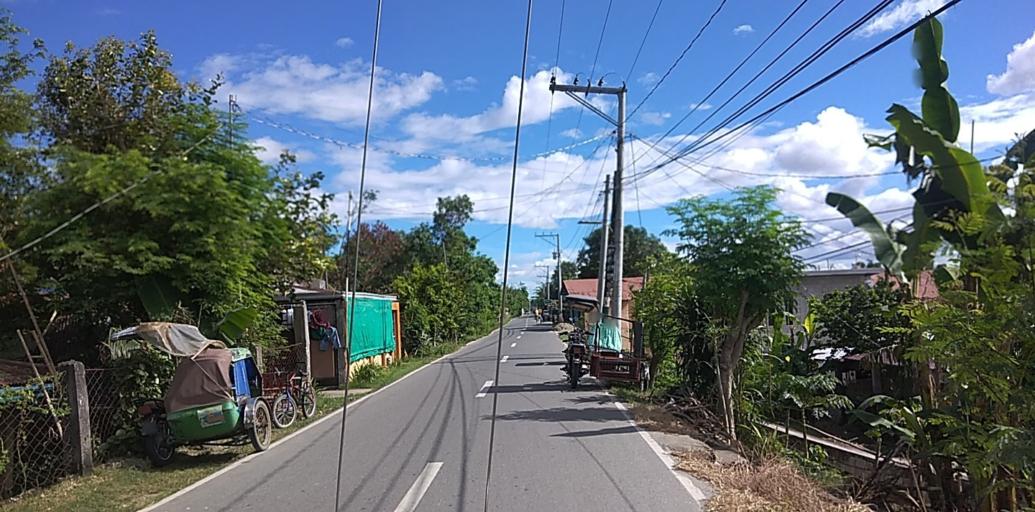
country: PH
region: Central Luzon
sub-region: Province of Pampanga
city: Arayat
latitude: 15.1371
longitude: 120.7843
